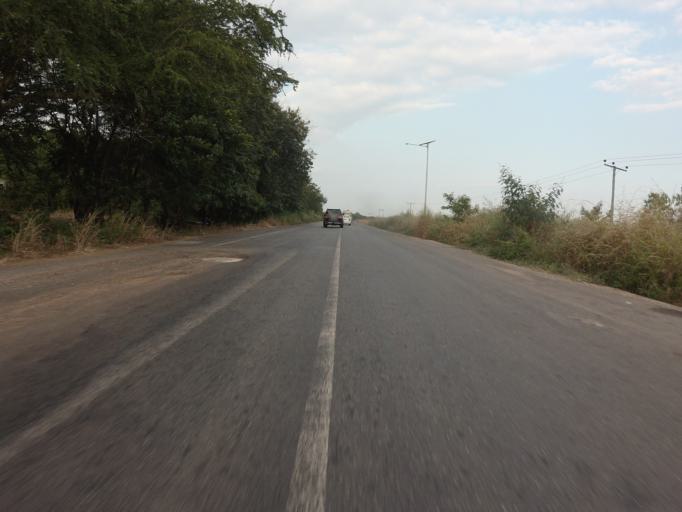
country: GH
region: Volta
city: Anloga
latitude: 6.0871
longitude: 0.5080
